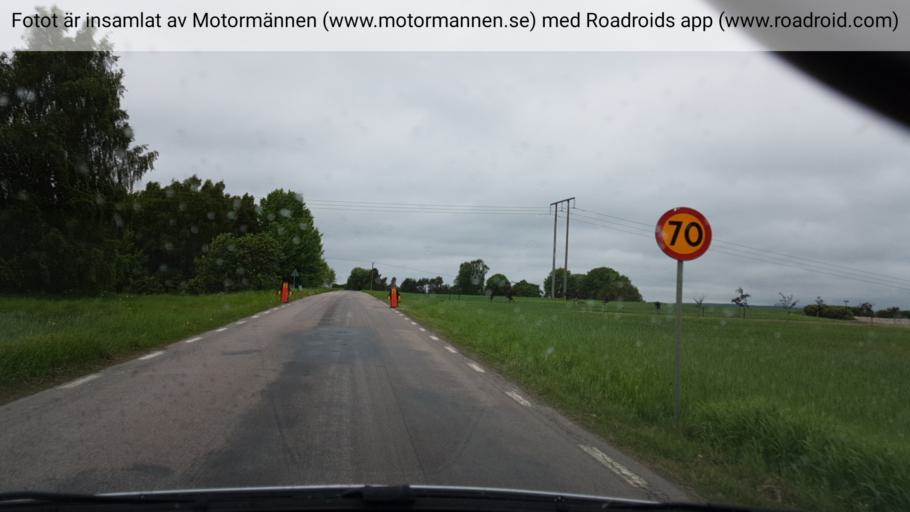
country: SE
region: Vaestra Goetaland
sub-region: Gotene Kommun
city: Kallby
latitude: 58.4968
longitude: 13.3136
